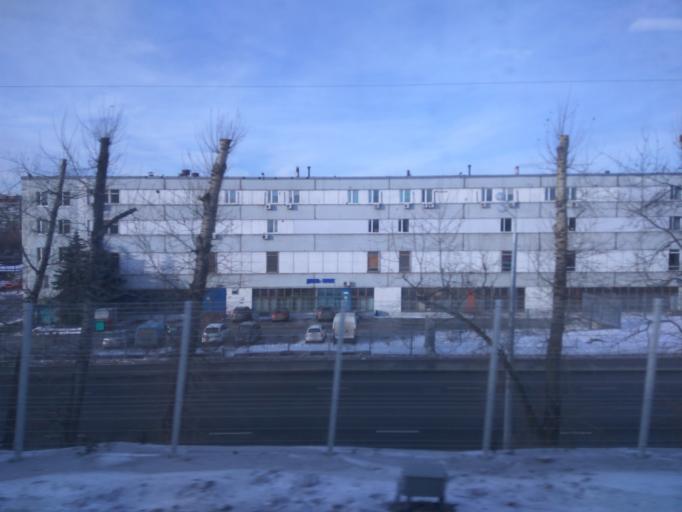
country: RU
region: Moskovskaya
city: Bogorodskoye
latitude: 55.7941
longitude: 37.7444
